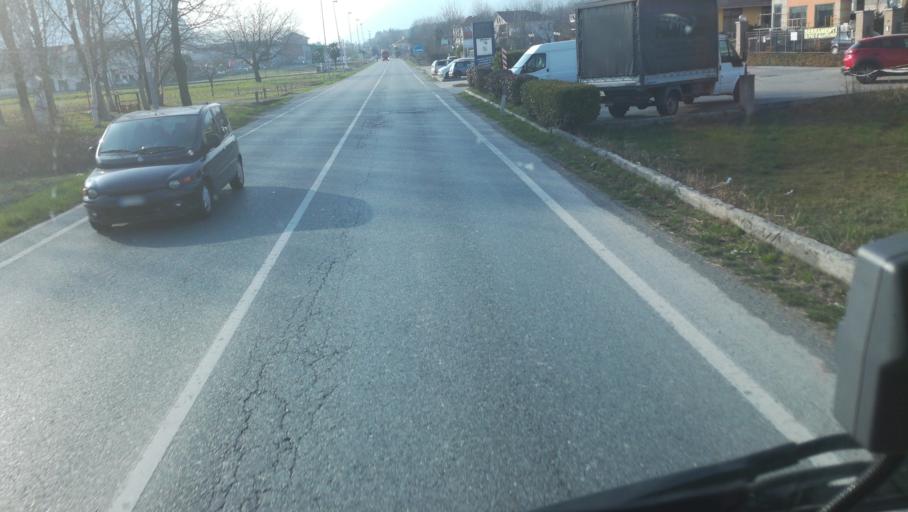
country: IT
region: Piedmont
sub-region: Provincia di Torino
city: Villar Dora
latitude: 45.1009
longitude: 7.3927
